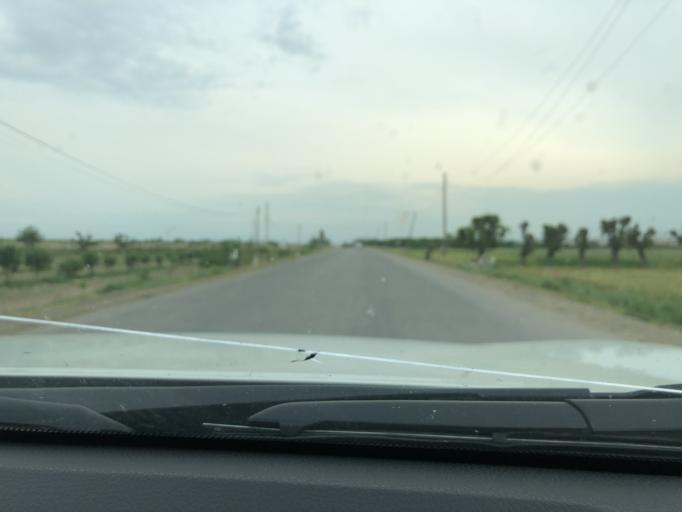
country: UZ
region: Toshkent
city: Bekobod
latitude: 40.1546
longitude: 69.2543
